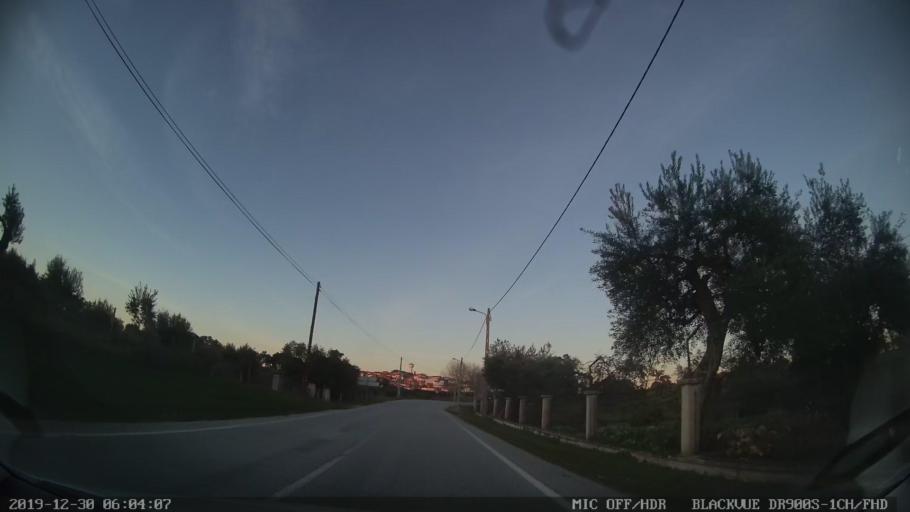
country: PT
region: Castelo Branco
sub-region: Penamacor
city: Penamacor
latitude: 40.0819
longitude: -7.2397
